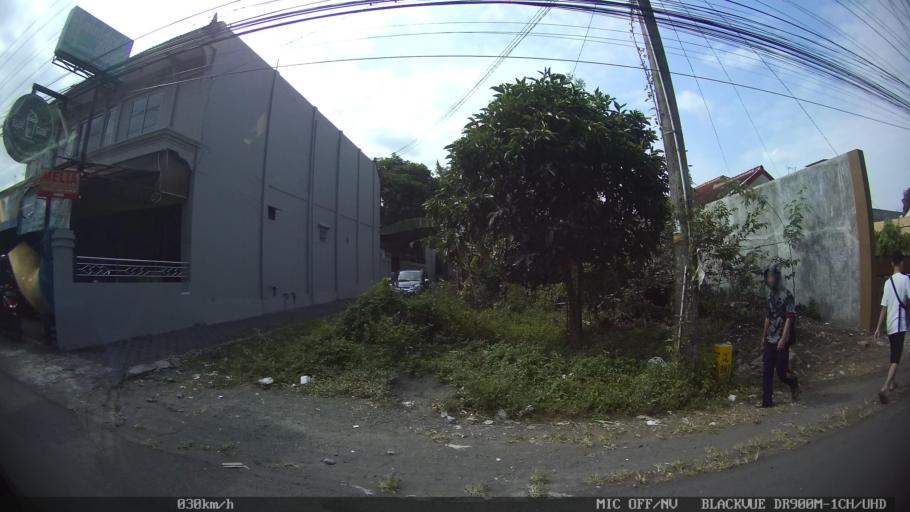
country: ID
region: Daerah Istimewa Yogyakarta
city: Depok
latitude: -7.7532
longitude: 110.4222
